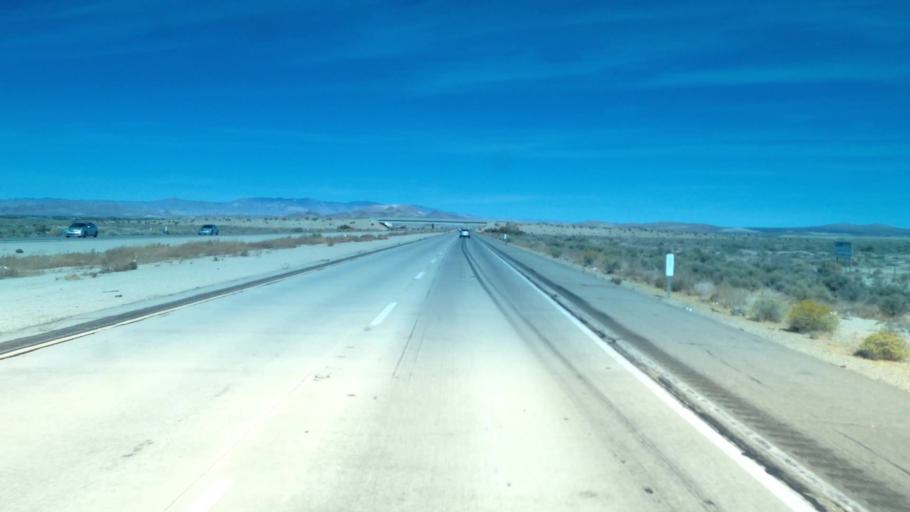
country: US
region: California
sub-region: Kern County
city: Rosamond
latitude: 34.7860
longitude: -118.1705
